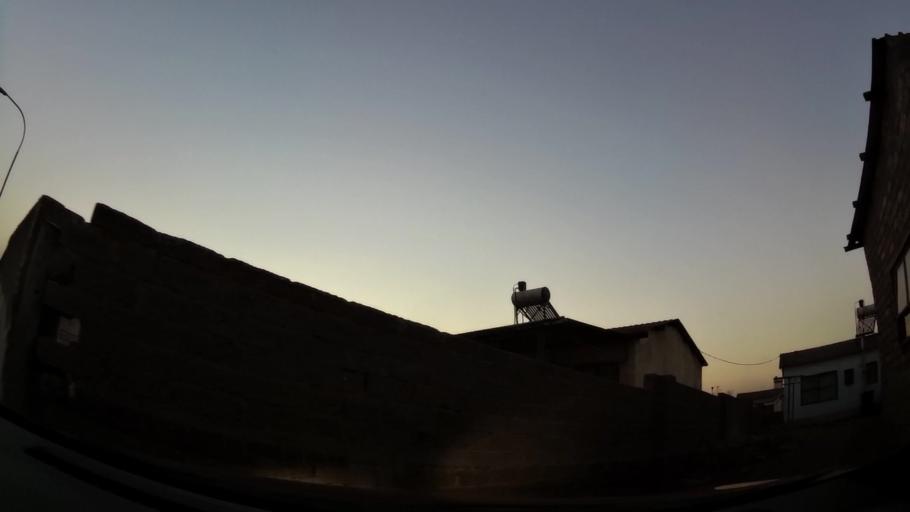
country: ZA
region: Gauteng
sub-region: City of Johannesburg Metropolitan Municipality
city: Soweto
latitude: -26.2945
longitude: 27.8705
